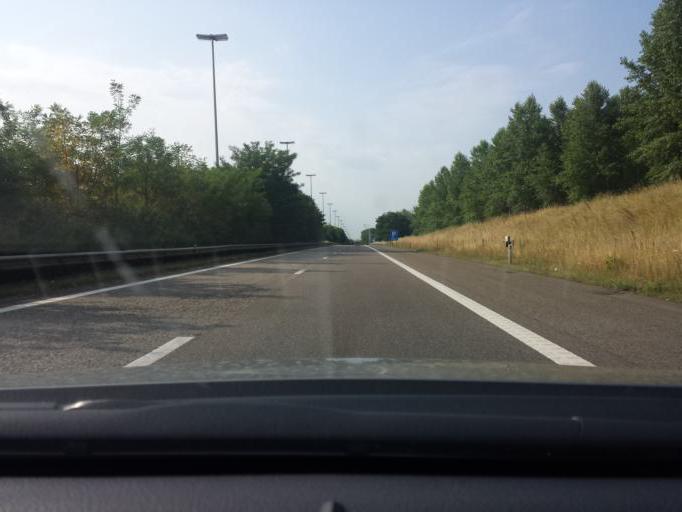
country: BE
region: Flanders
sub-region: Provincie Limburg
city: Hoeselt
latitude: 50.8430
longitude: 5.5066
